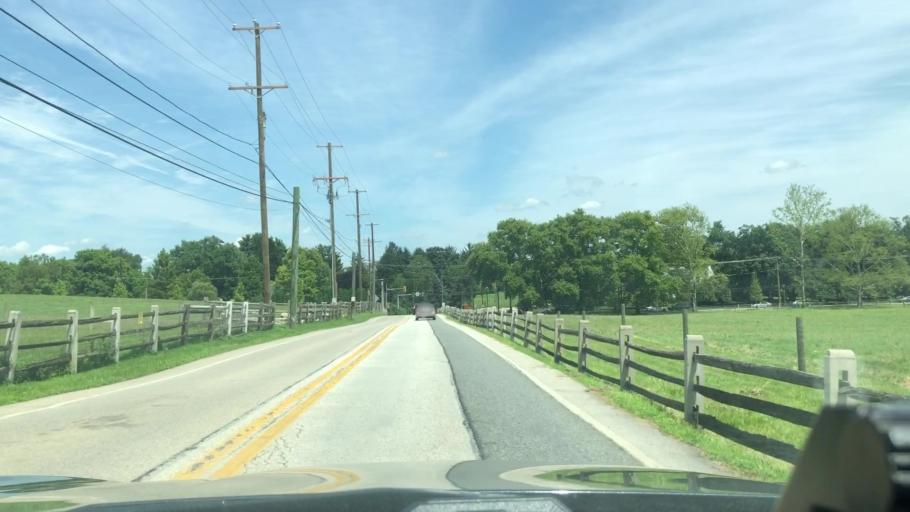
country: US
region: Pennsylvania
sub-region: Montgomery County
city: Flourtown
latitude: 40.1028
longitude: -75.2353
